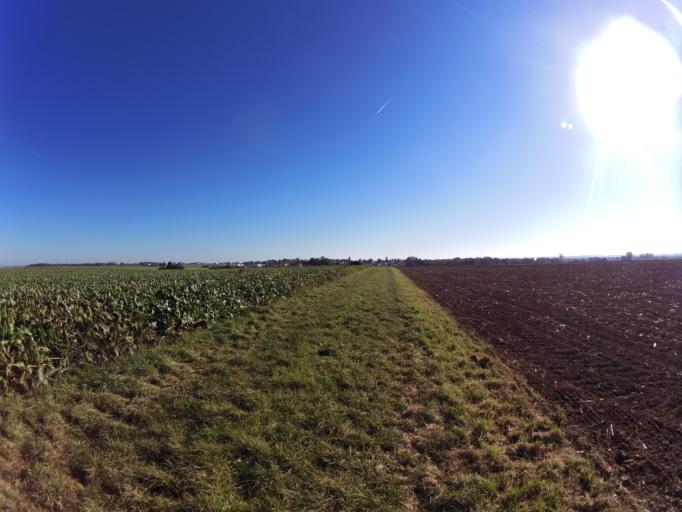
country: DE
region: Bavaria
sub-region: Regierungsbezirk Unterfranken
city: Giebelstadt
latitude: 49.6645
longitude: 9.9368
